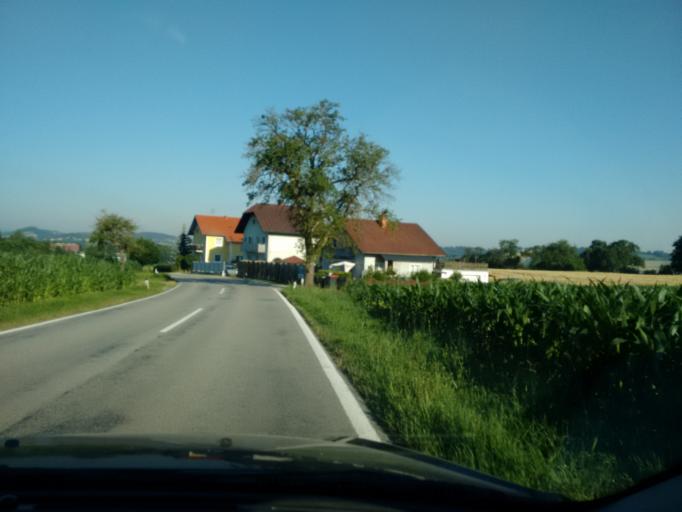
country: AT
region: Upper Austria
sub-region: Politischer Bezirk Grieskirchen
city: Bad Schallerbach
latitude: 48.1929
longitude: 13.9376
